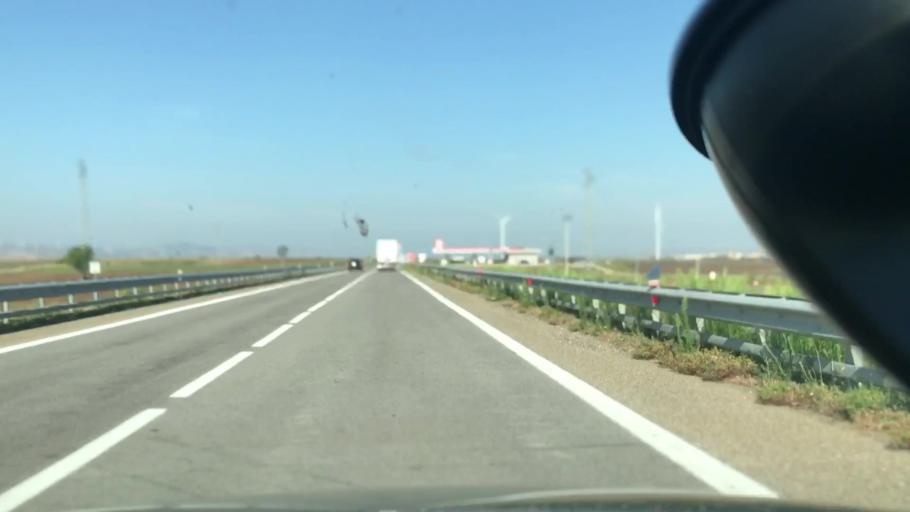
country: IT
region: Basilicate
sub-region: Provincia di Potenza
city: Lavello
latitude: 41.0161
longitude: 15.8190
